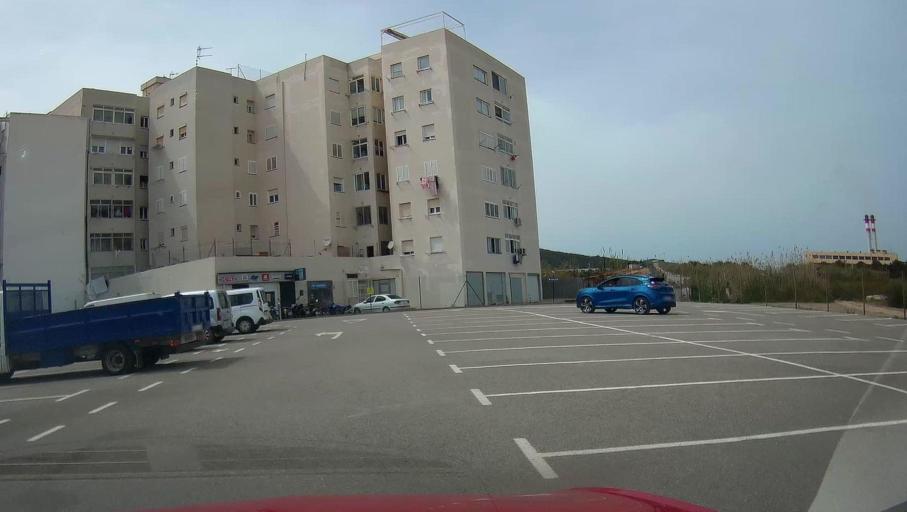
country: ES
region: Balearic Islands
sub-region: Illes Balears
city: Ibiza
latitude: 38.9140
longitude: 1.4314
